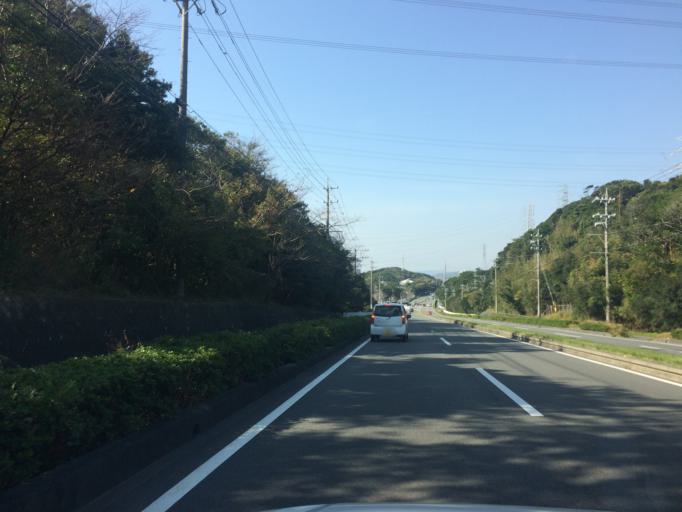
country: JP
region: Shizuoka
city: Oyama
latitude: 34.6265
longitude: 138.1493
